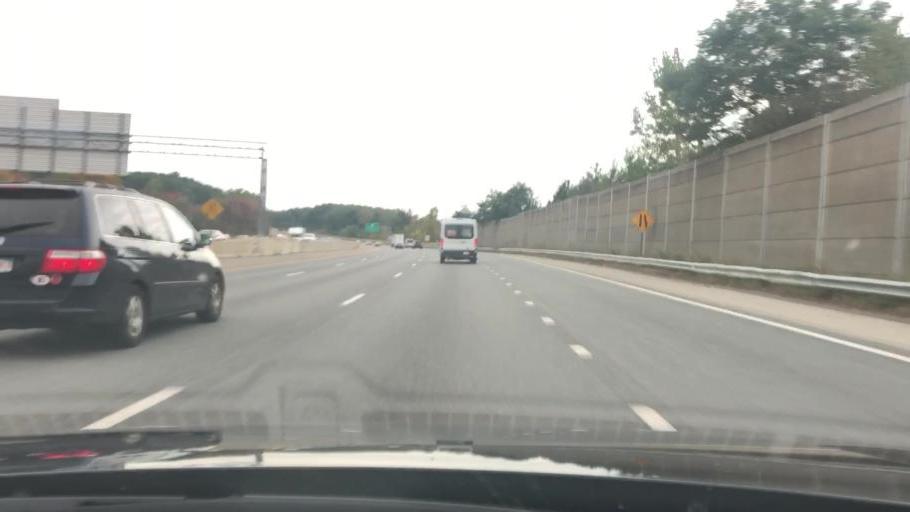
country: US
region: Massachusetts
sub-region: Middlesex County
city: Lowell
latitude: 42.6195
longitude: -71.3369
